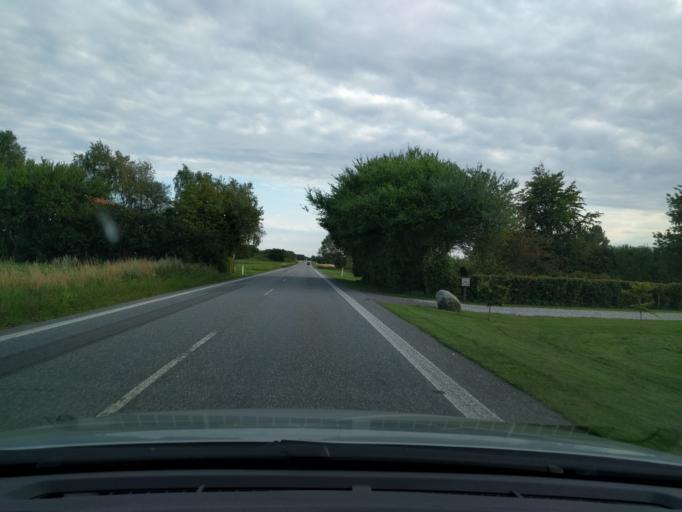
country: DK
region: Zealand
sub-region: Guldborgsund Kommune
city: Stubbekobing
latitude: 54.8209
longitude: 11.9942
